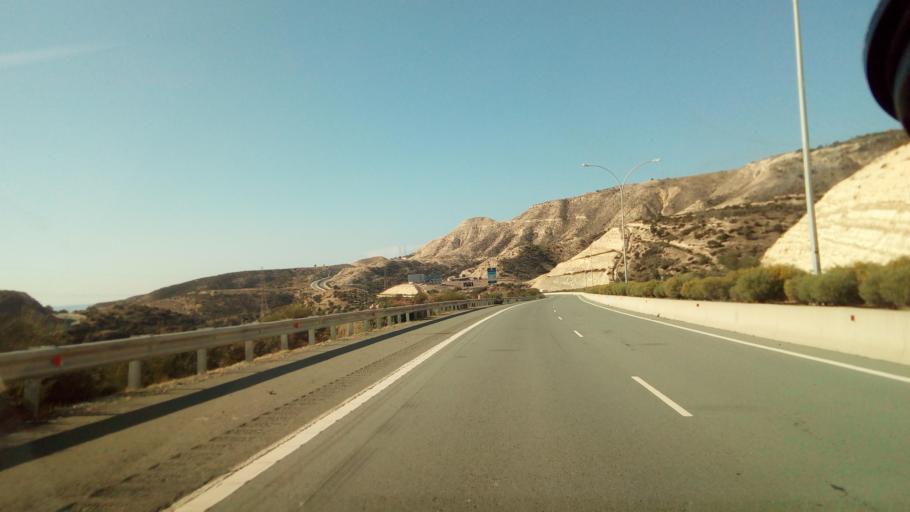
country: CY
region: Limassol
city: Pissouri
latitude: 34.6732
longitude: 32.6655
